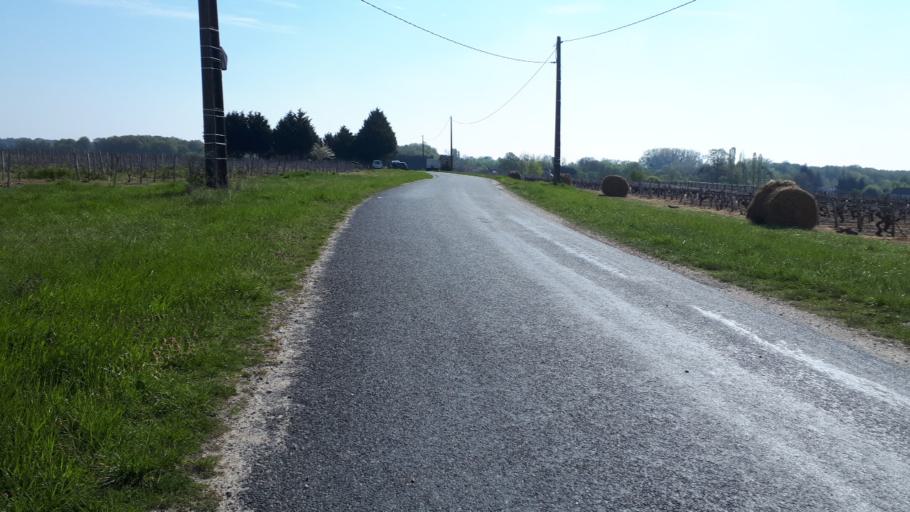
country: FR
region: Centre
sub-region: Departement du Loir-et-Cher
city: Saint-Romain-sur-Cher
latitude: 47.3660
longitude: 1.3907
